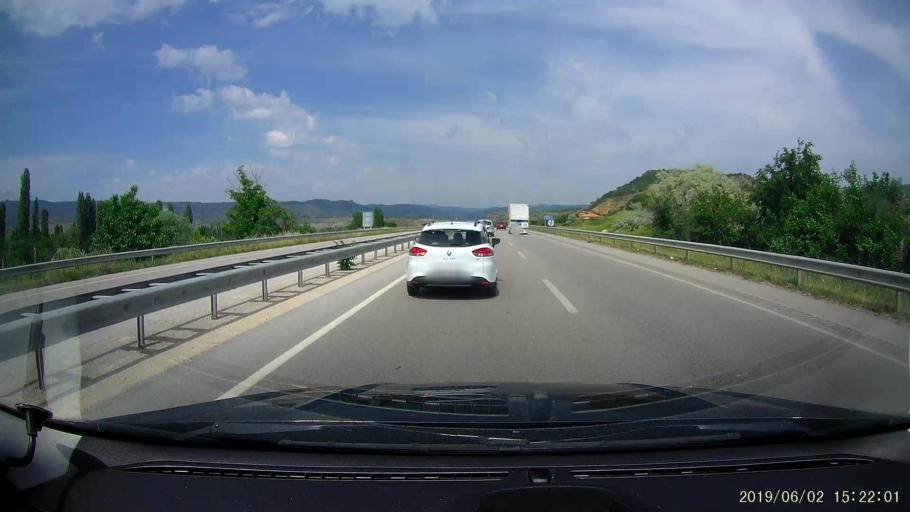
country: TR
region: Corum
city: Osmancik
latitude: 40.9803
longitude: 34.9488
